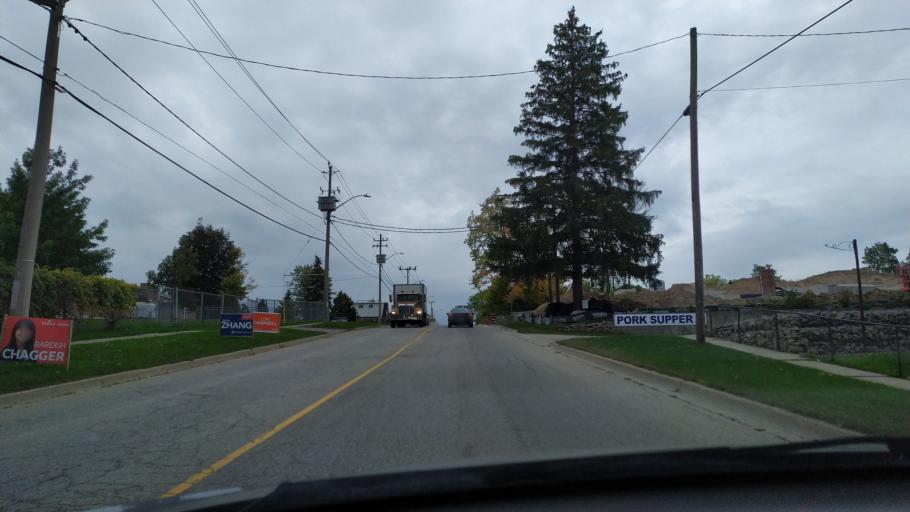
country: CA
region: Ontario
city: Waterloo
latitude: 43.4831
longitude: -80.4852
